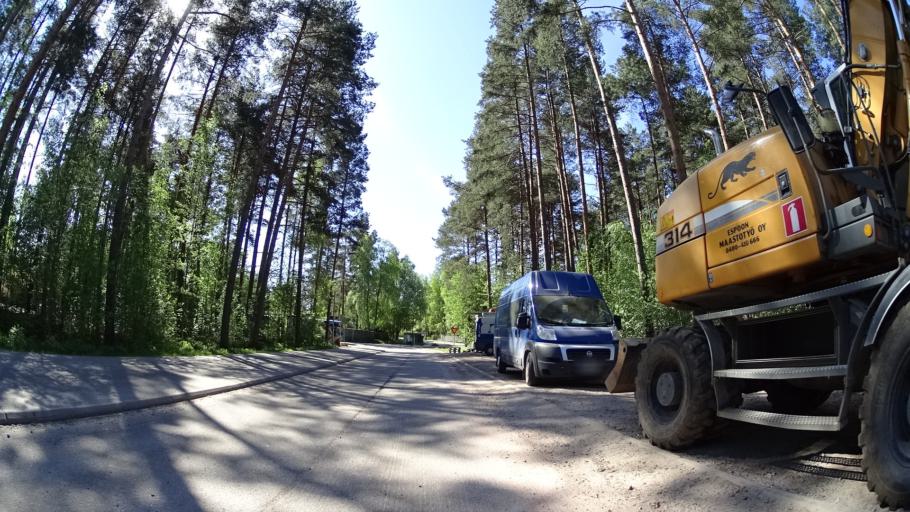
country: FI
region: Uusimaa
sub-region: Helsinki
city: Espoo
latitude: 60.1636
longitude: 24.6765
